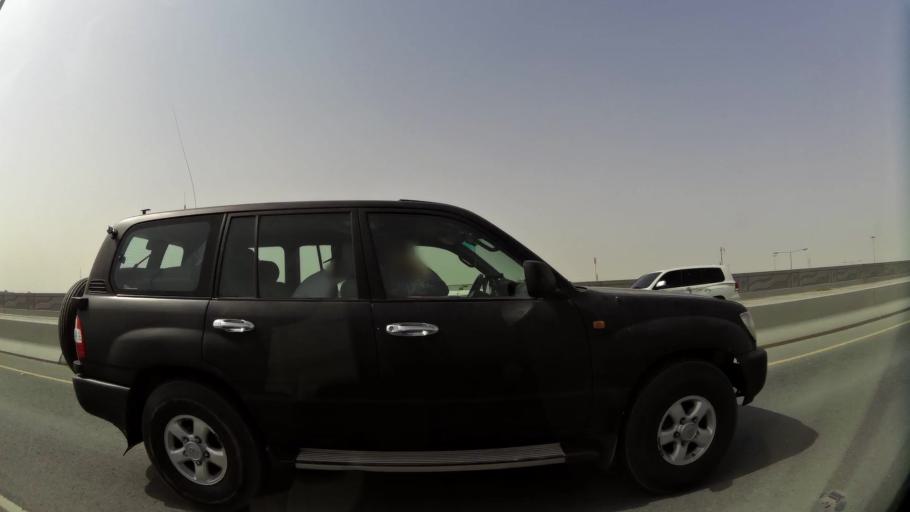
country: QA
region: Baladiyat ar Rayyan
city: Ar Rayyan
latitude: 25.2248
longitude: 51.4310
